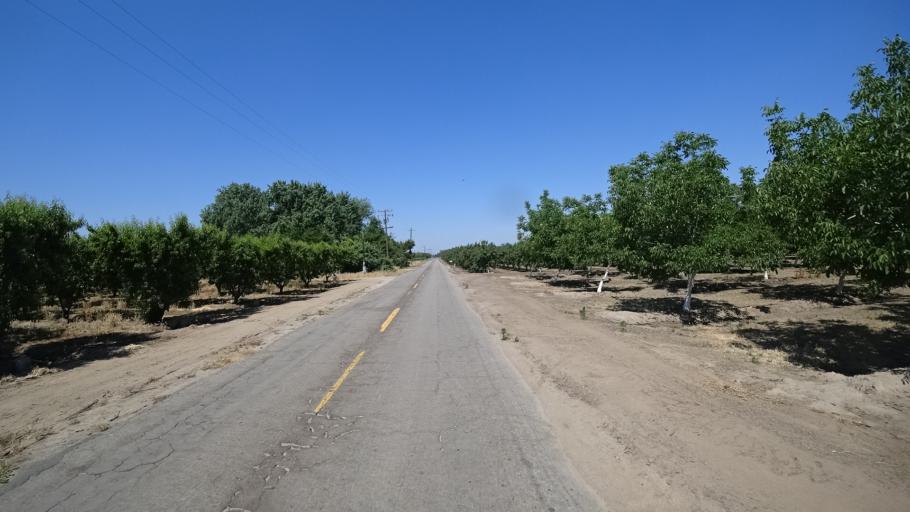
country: US
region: California
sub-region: Fresno County
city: Kingsburg
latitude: 36.4741
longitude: -119.5592
